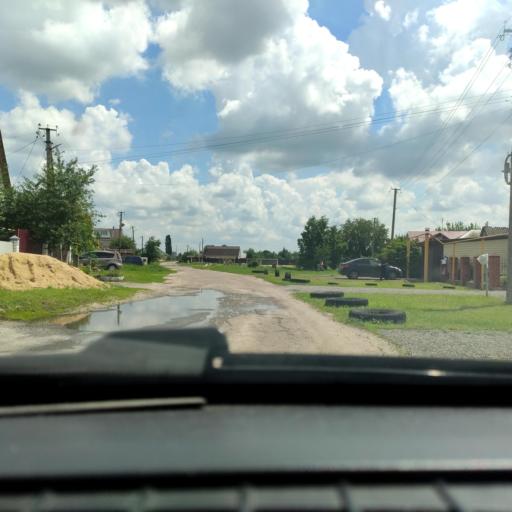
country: RU
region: Voronezj
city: Novaya Usman'
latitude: 51.6213
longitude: 39.3764
